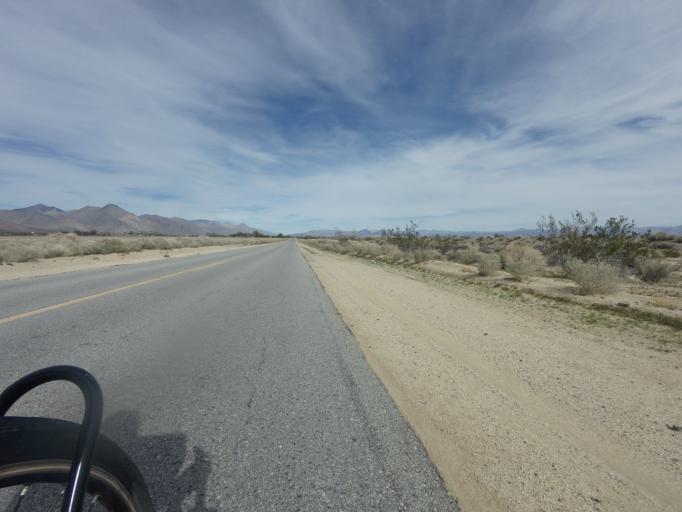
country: US
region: California
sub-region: Kern County
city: Inyokern
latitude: 35.7192
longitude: -117.8338
